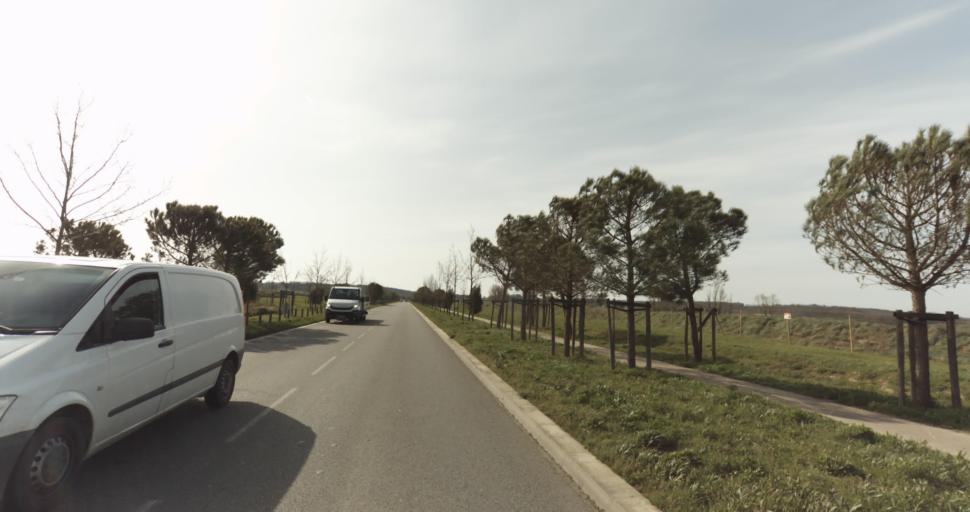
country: FR
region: Midi-Pyrenees
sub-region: Departement du Tarn
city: Saint-Sulpice-la-Pointe
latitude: 43.7619
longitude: 1.6577
